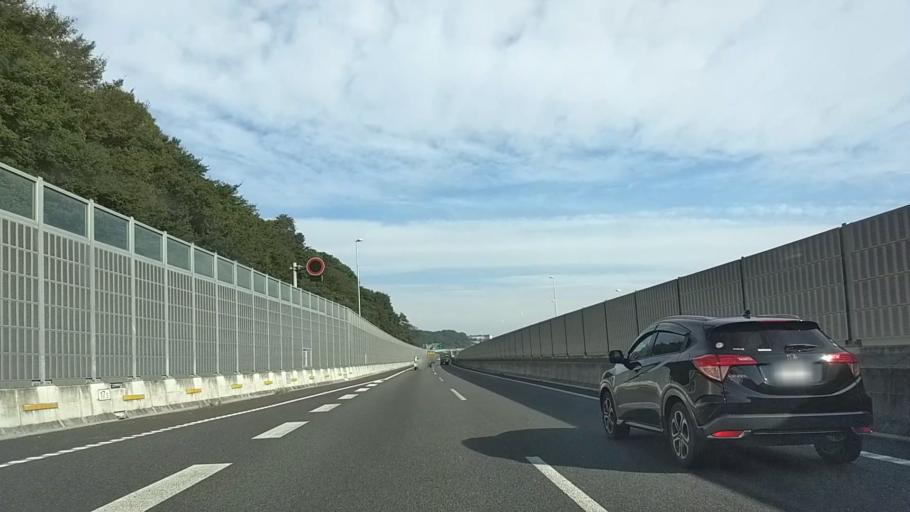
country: JP
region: Kanagawa
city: Zama
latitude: 35.4916
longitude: 139.3685
